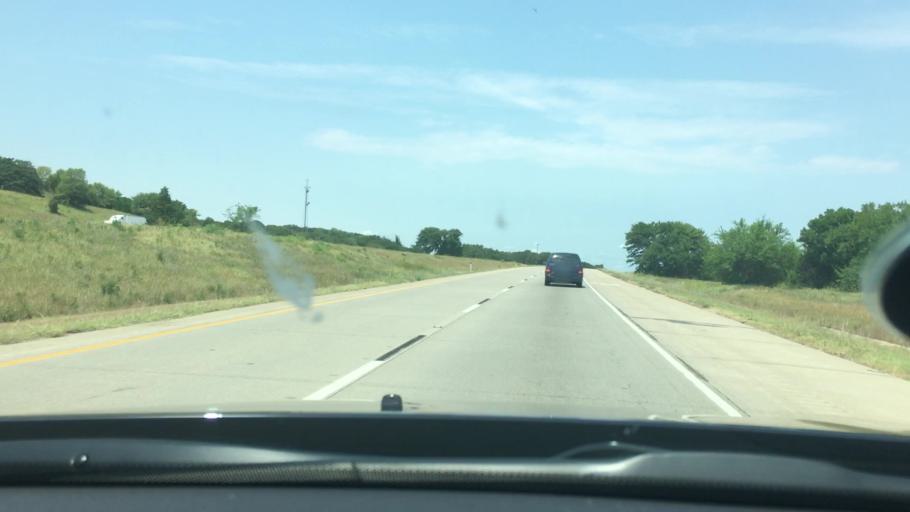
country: US
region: Oklahoma
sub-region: Love County
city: Marietta
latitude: 33.9935
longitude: -97.1395
